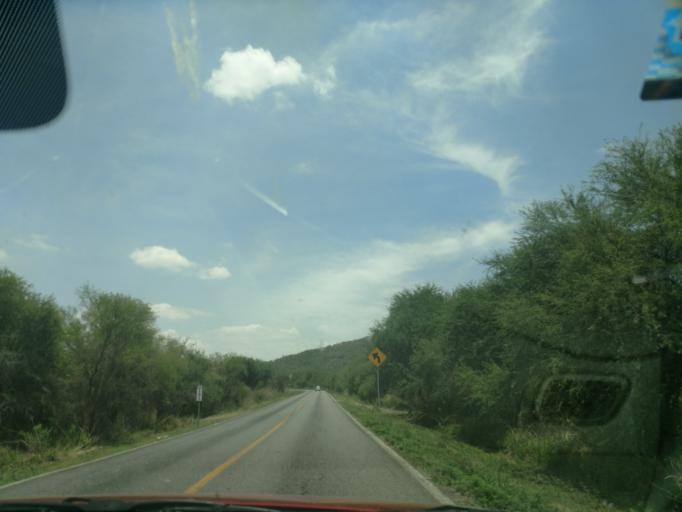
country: MX
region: San Luis Potosi
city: Ciudad Fernandez
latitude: 21.9957
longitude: -100.1378
